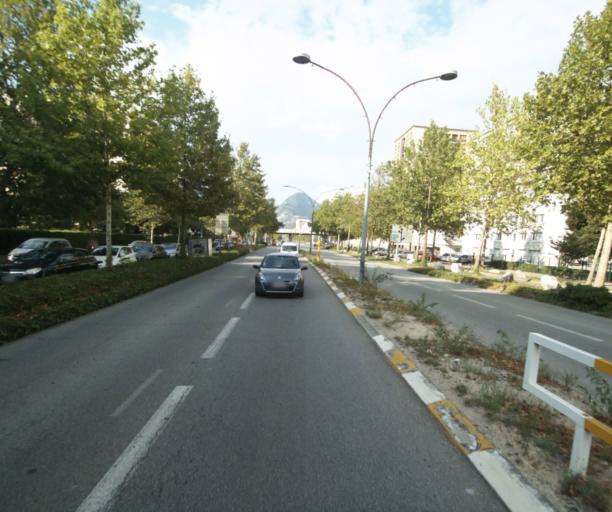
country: FR
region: Rhone-Alpes
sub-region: Departement de l'Isere
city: Grenoble
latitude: 45.1627
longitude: 5.7105
